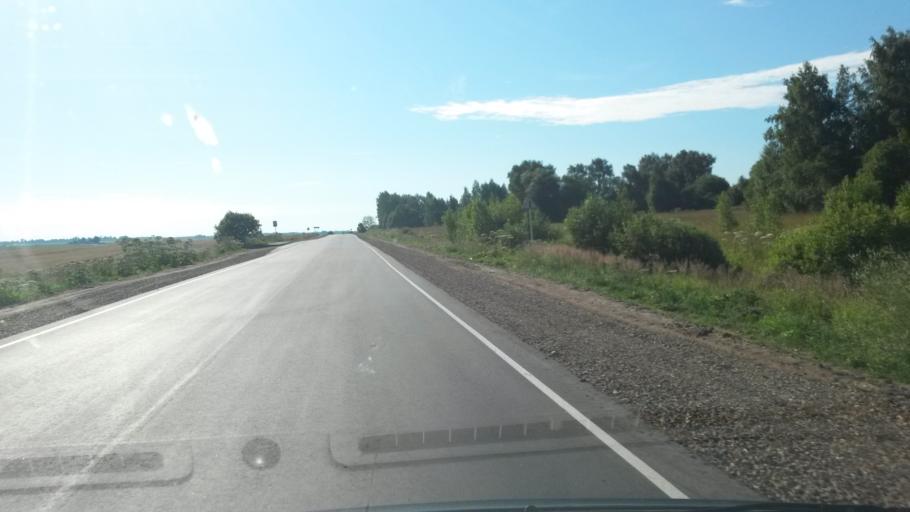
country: RU
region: Jaroslavl
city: Dubki
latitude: 57.1932
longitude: 40.3629
